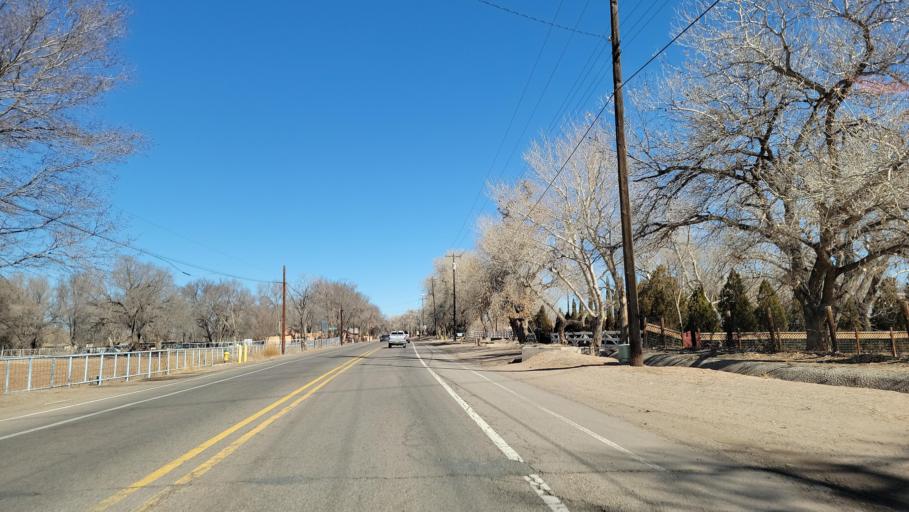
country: US
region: New Mexico
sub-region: Bernalillo County
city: South Valley
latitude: 35.0046
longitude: -106.6899
